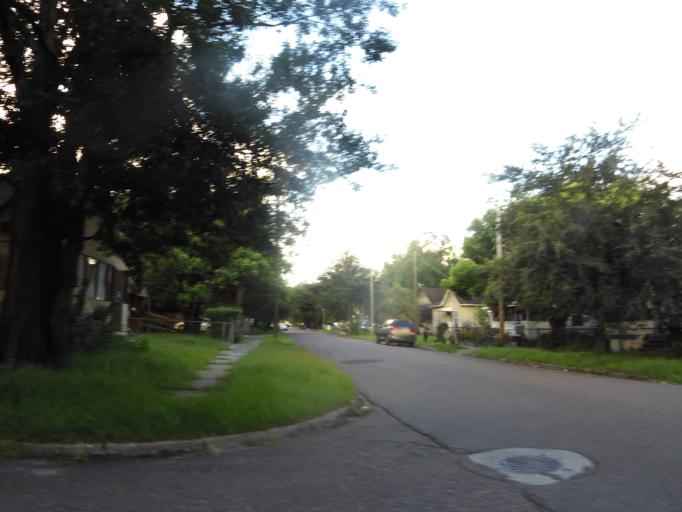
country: US
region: Florida
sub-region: Duval County
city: Jacksonville
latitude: 30.3405
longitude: -81.6844
